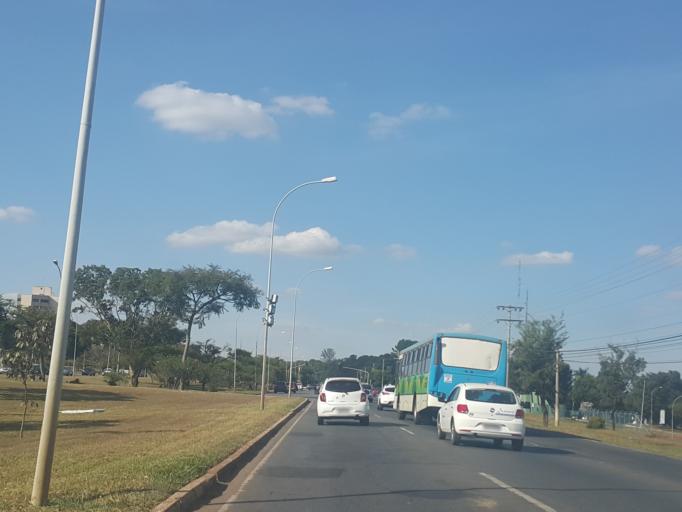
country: BR
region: Federal District
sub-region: Brasilia
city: Brasilia
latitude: -15.8091
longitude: -47.9344
